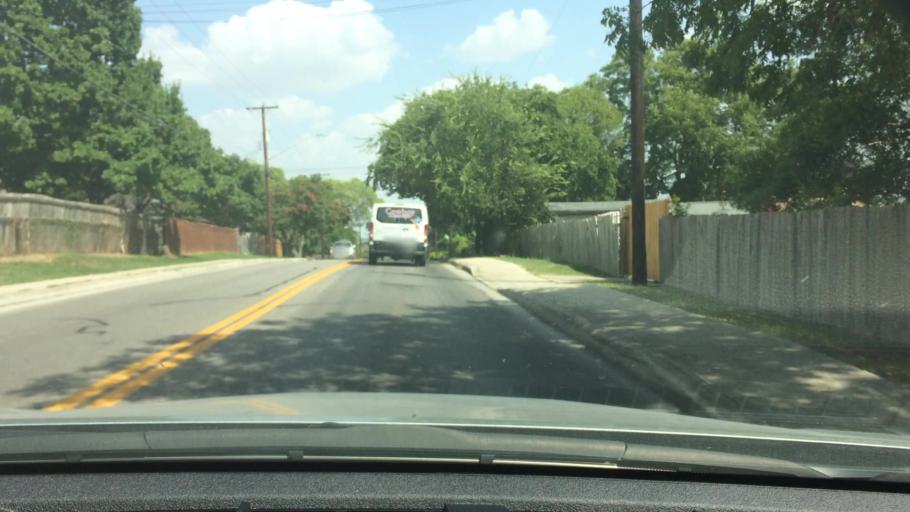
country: US
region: Texas
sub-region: Bexar County
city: Castle Hills
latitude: 29.5340
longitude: -98.5001
